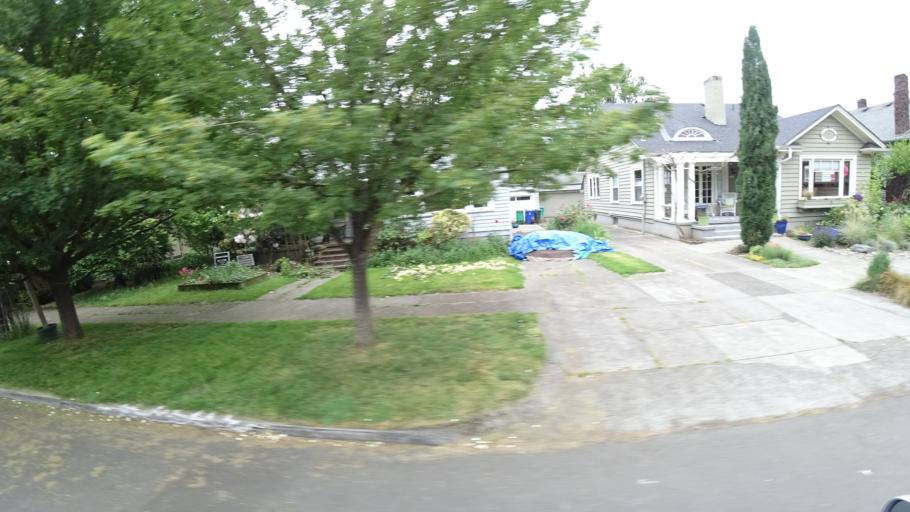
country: US
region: Oregon
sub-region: Multnomah County
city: Portland
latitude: 45.5393
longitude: -122.6069
